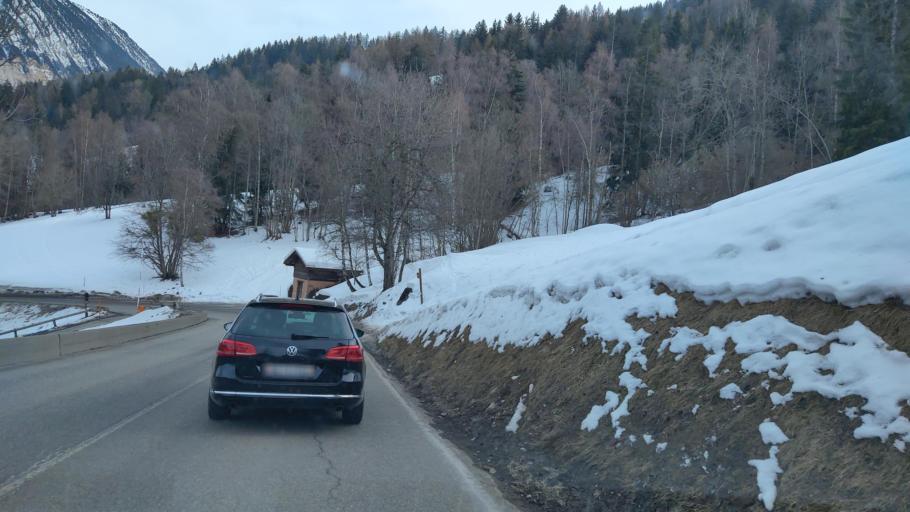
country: FR
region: Rhone-Alpes
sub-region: Departement de la Savoie
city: Saint-Bon-Tarentaise
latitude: 45.4327
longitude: 6.6331
